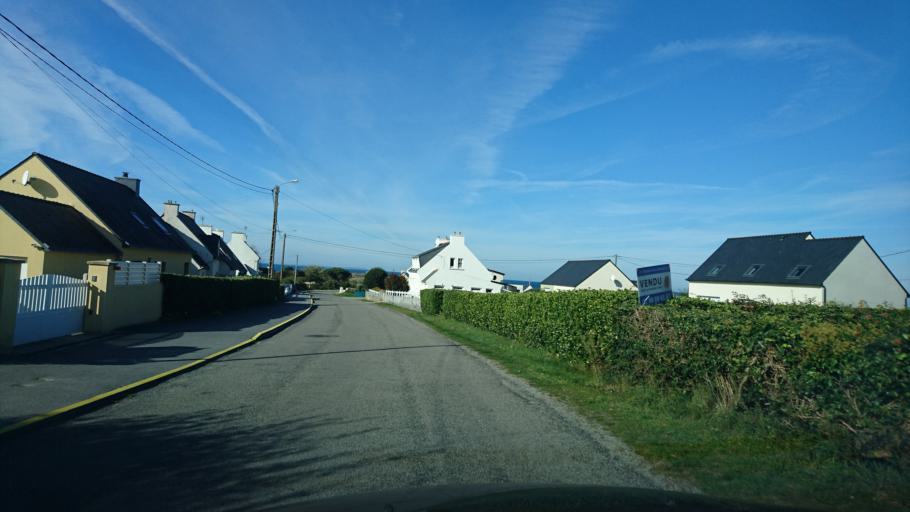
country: FR
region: Brittany
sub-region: Departement du Finistere
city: Lampaul-Plouarzel
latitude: 48.4364
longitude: -4.7757
